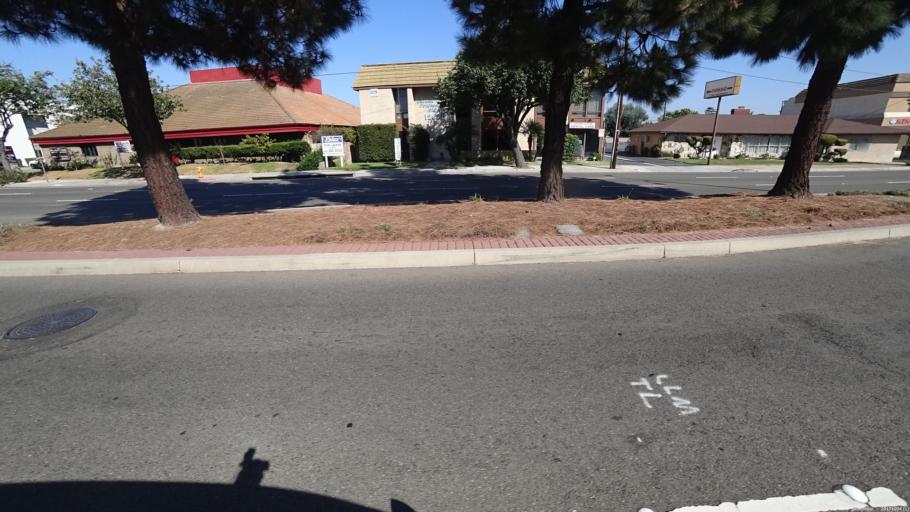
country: US
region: California
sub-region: Orange County
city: Garden Grove
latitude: 33.7794
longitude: -117.9585
